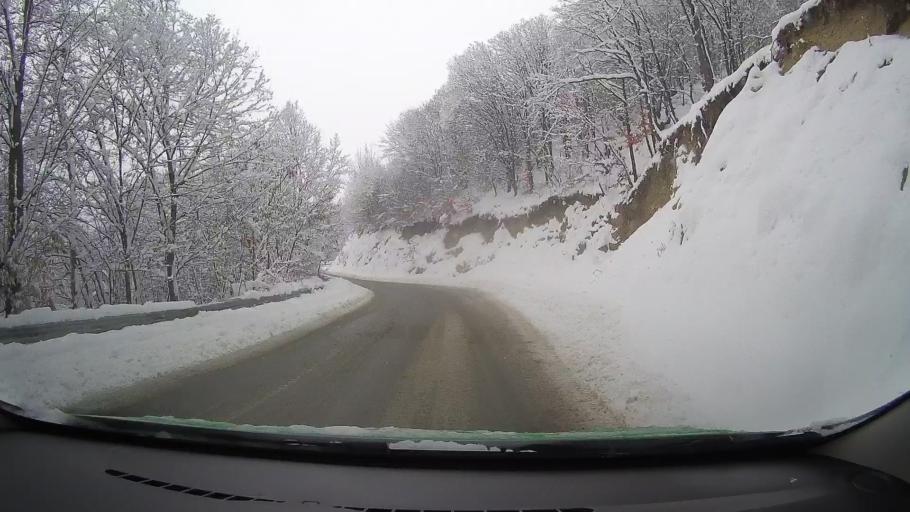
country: RO
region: Sibiu
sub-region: Comuna Jina
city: Jina
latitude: 45.7689
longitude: 23.6700
